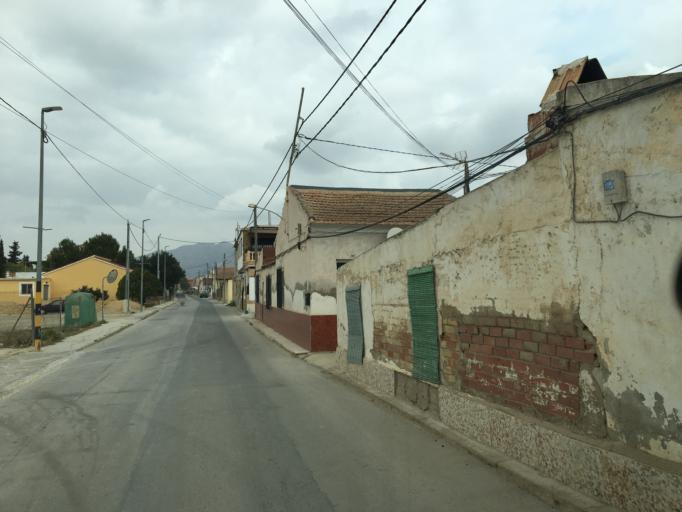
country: ES
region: Murcia
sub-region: Murcia
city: Beniel
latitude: 38.0428
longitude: -0.9915
